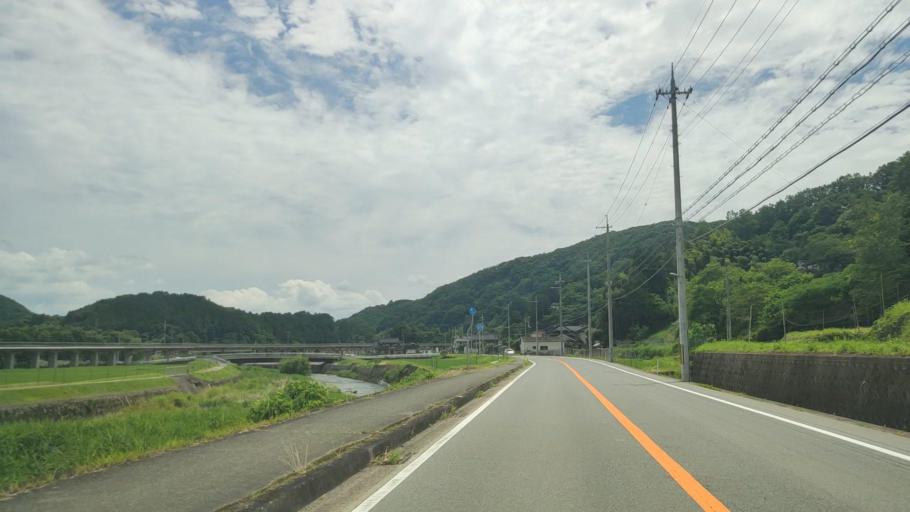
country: JP
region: Hyogo
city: Yamazakicho-nakabirose
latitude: 35.0388
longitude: 134.3684
